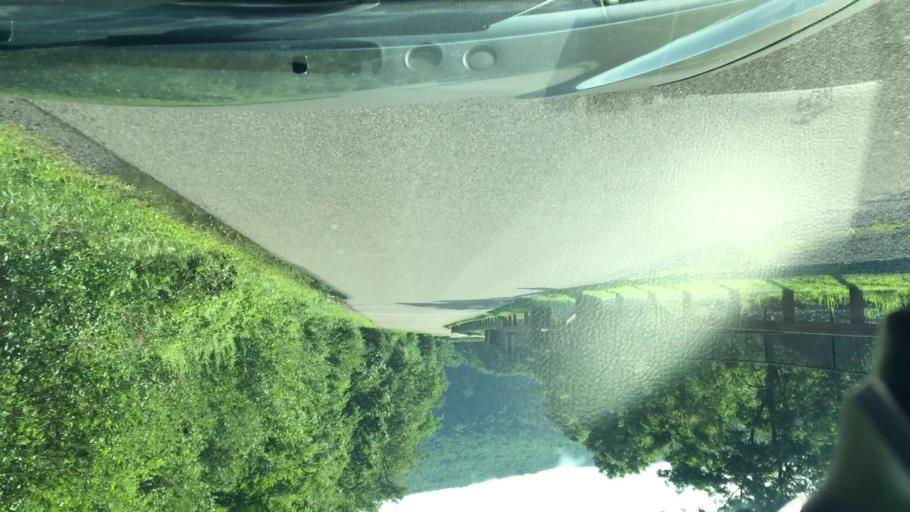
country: US
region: Pennsylvania
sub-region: Carbon County
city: Jim Thorpe
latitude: 40.8759
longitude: -75.7583
